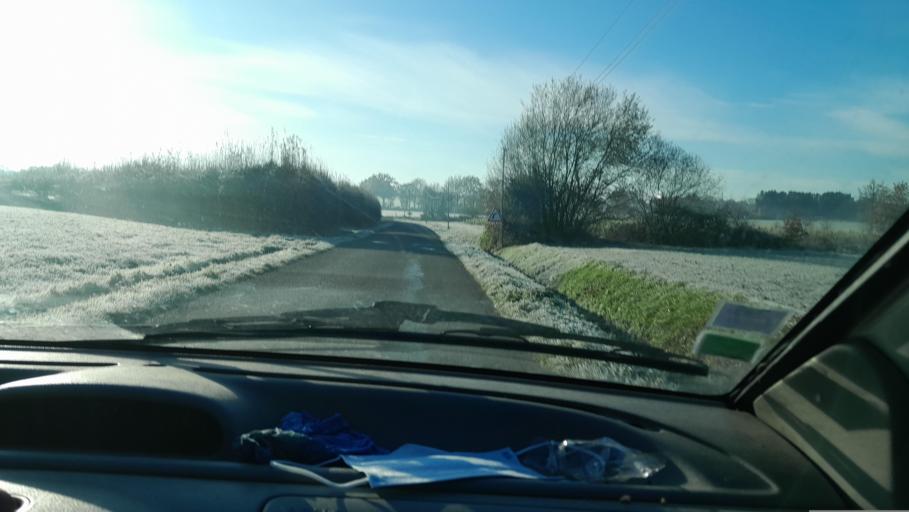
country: FR
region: Brittany
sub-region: Departement d'Ille-et-Vilaine
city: Rannee
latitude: 47.8832
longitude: -1.1804
